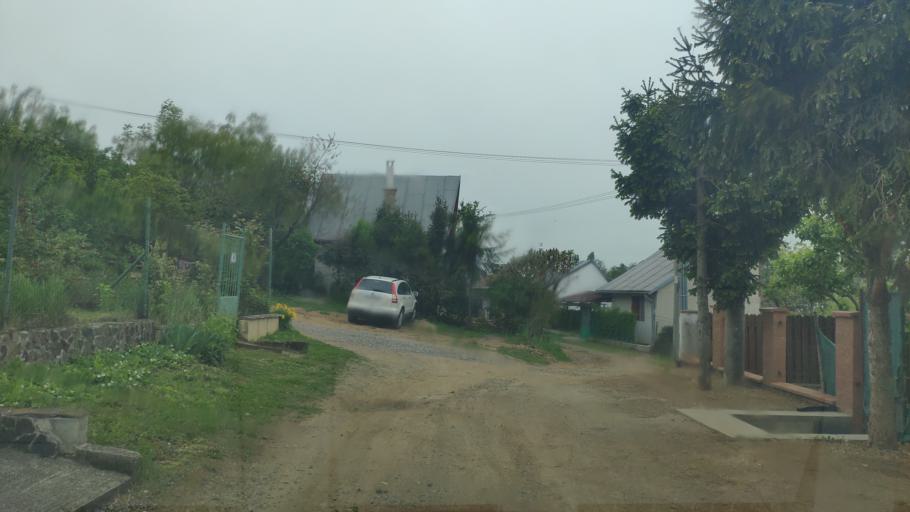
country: SK
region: Kosicky
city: Kosice
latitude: 48.6342
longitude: 21.1791
